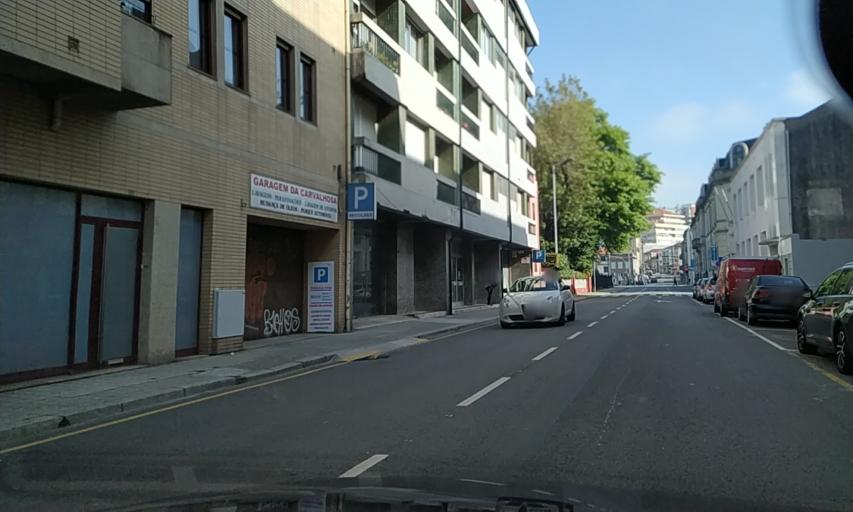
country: PT
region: Porto
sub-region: Porto
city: Porto
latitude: 41.1542
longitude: -8.6210
